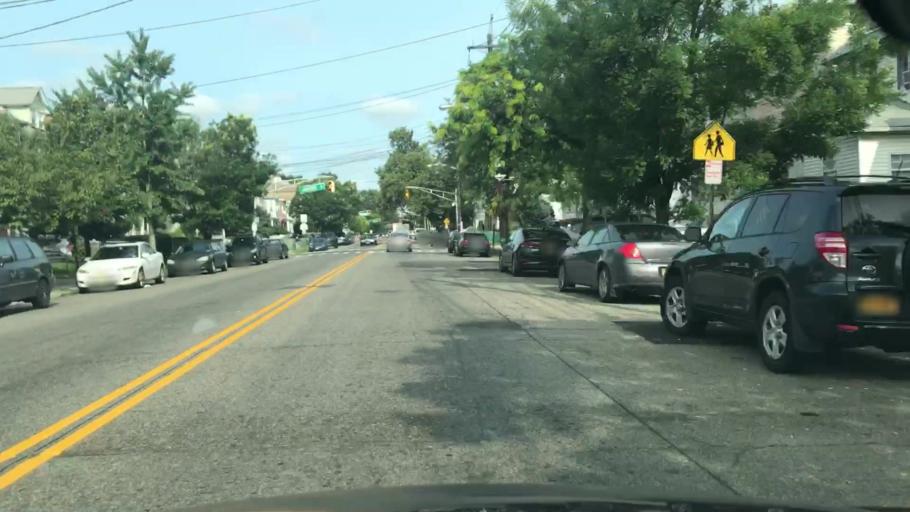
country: US
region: New Jersey
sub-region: Union County
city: Elizabeth
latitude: 40.6787
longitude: -74.2001
